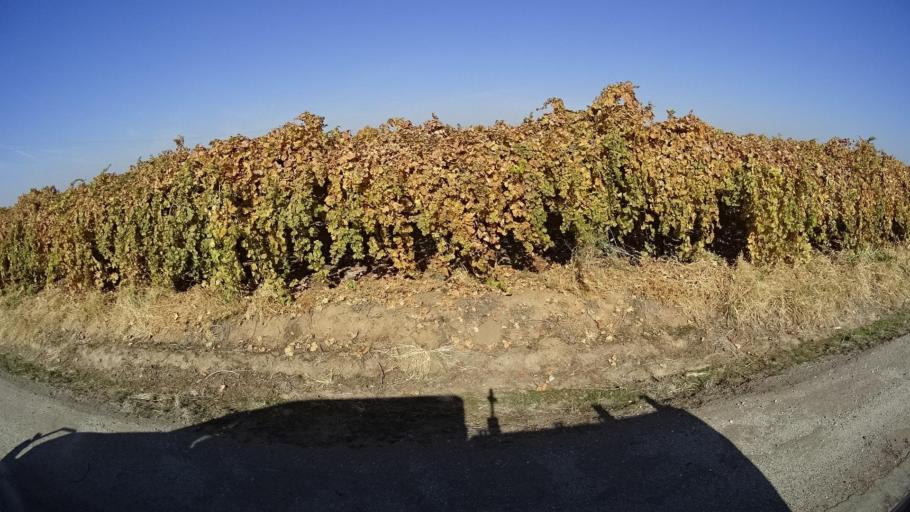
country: US
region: California
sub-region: Kern County
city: McFarland
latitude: 35.7035
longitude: -119.1554
